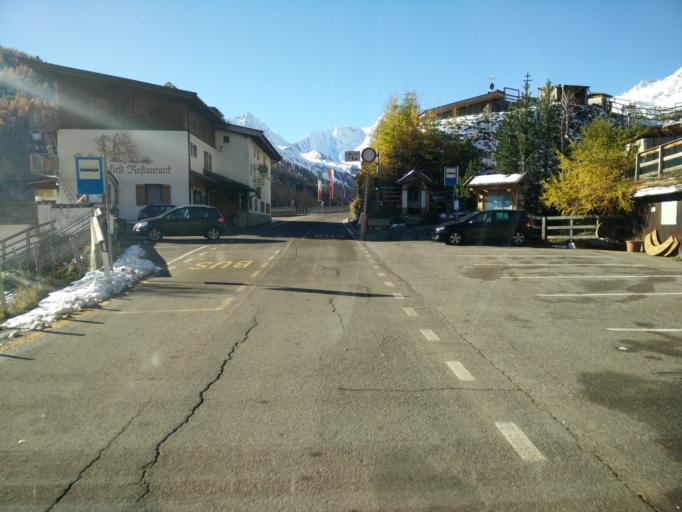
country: IT
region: Trentino-Alto Adige
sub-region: Bolzano
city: Moso in Passiria
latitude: 46.8884
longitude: 11.1269
